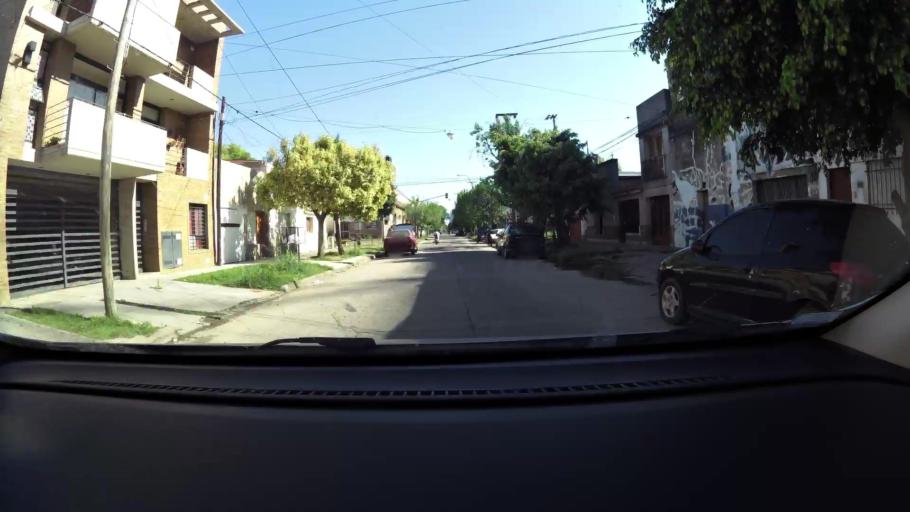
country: AR
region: Santa Fe
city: Santa Fe de la Vera Cruz
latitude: -31.6245
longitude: -60.6940
